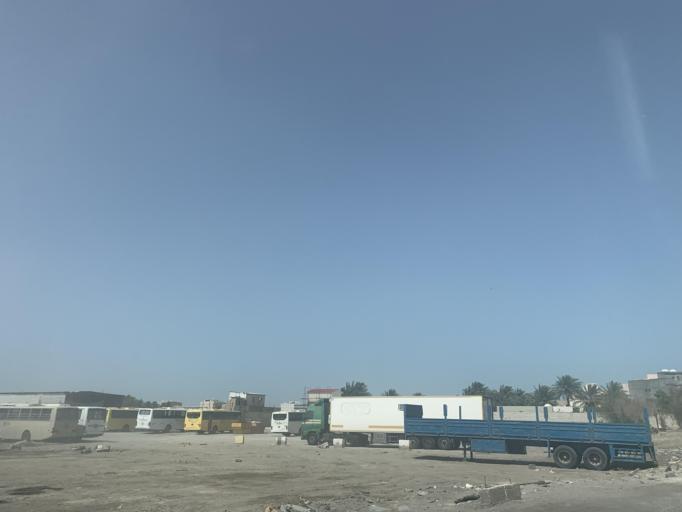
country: BH
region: Northern
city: Sitrah
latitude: 26.1702
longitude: 50.6129
